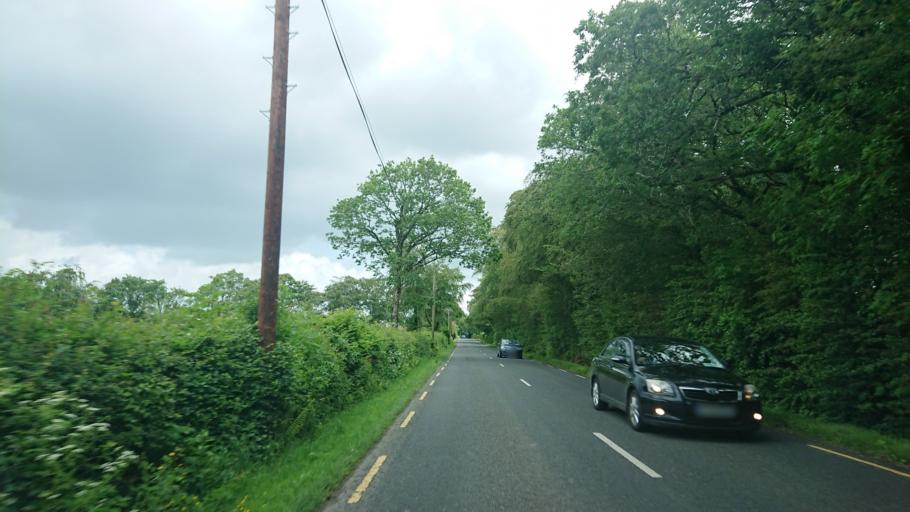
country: IE
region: Leinster
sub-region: Kilkenny
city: Graiguenamanagh
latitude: 52.4721
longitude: -6.9549
